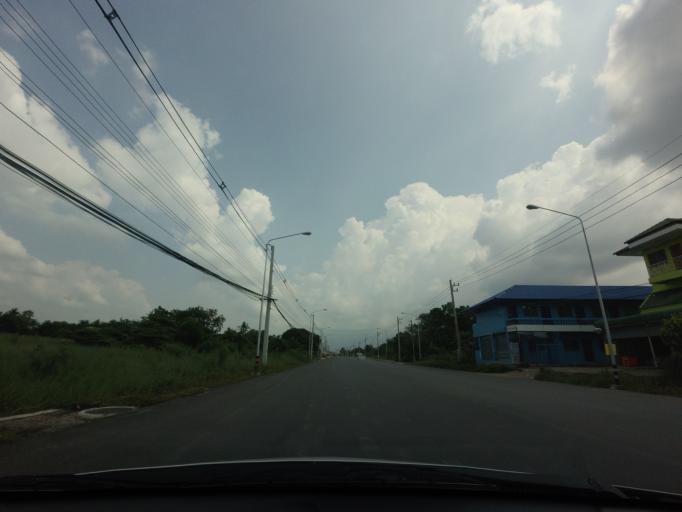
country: TH
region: Nakhon Pathom
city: Nakhon Chai Si
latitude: 13.8042
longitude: 100.2104
